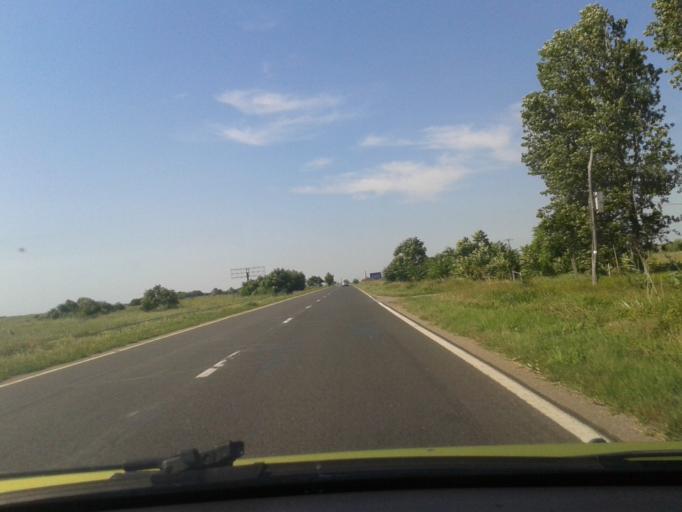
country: RO
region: Constanta
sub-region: Municipiul Mangalia
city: Mangalia
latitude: 43.7720
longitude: 28.5763
